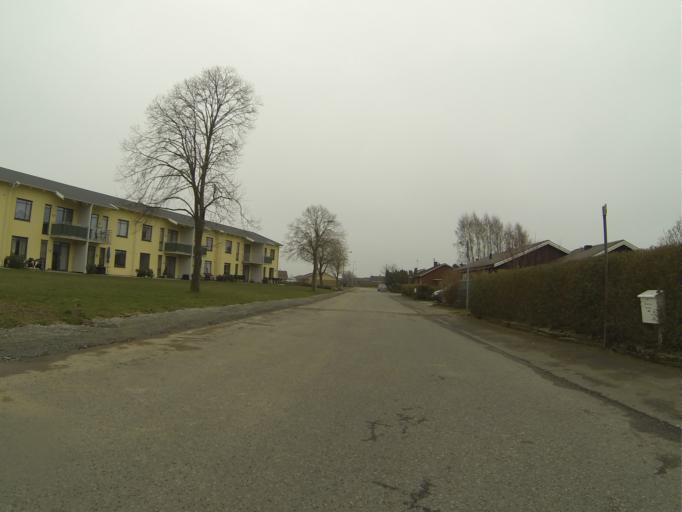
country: SE
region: Skane
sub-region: Simrishamns Kommun
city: Kivik
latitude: 55.5442
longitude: 14.1880
